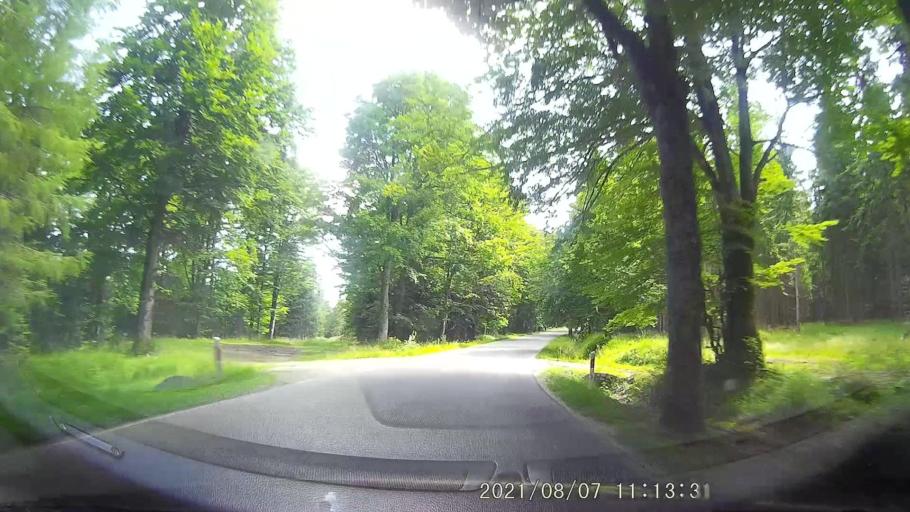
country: PL
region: Lower Silesian Voivodeship
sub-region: Powiat klodzki
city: Bystrzyca Klodzka
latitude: 50.2761
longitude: 16.5239
